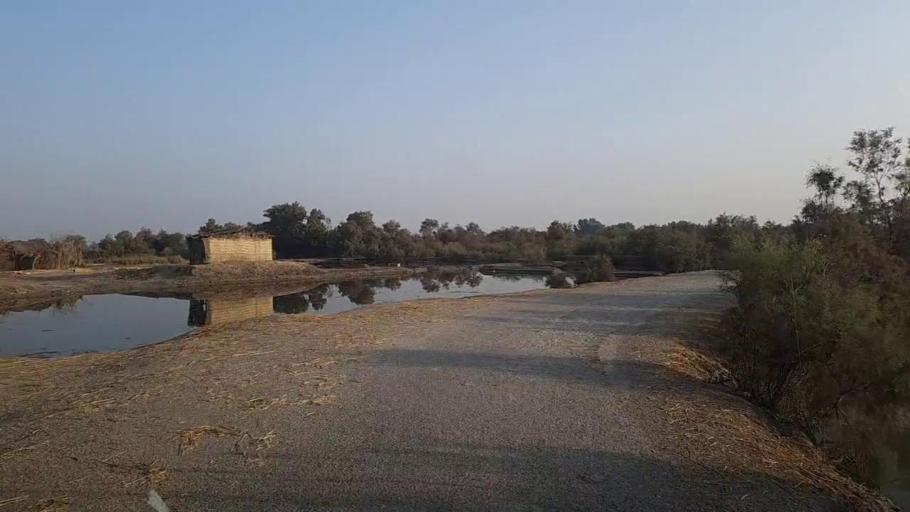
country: PK
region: Sindh
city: Kandhkot
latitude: 28.2395
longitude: 69.0932
